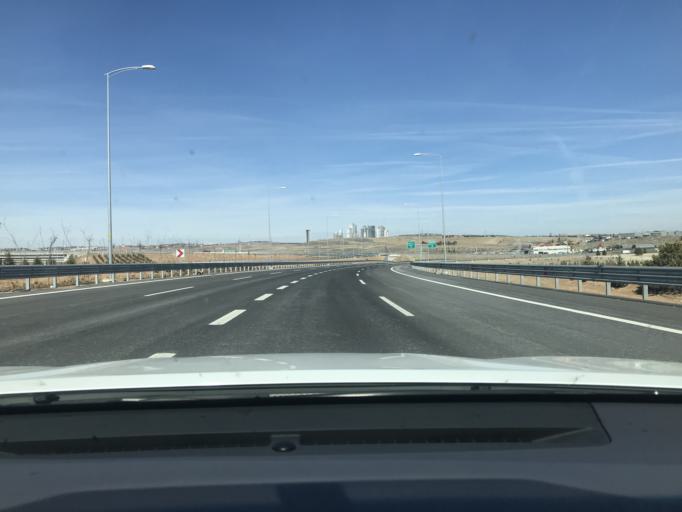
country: TR
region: Ankara
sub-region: Goelbasi
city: Golbasi
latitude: 39.7837
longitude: 32.7452
